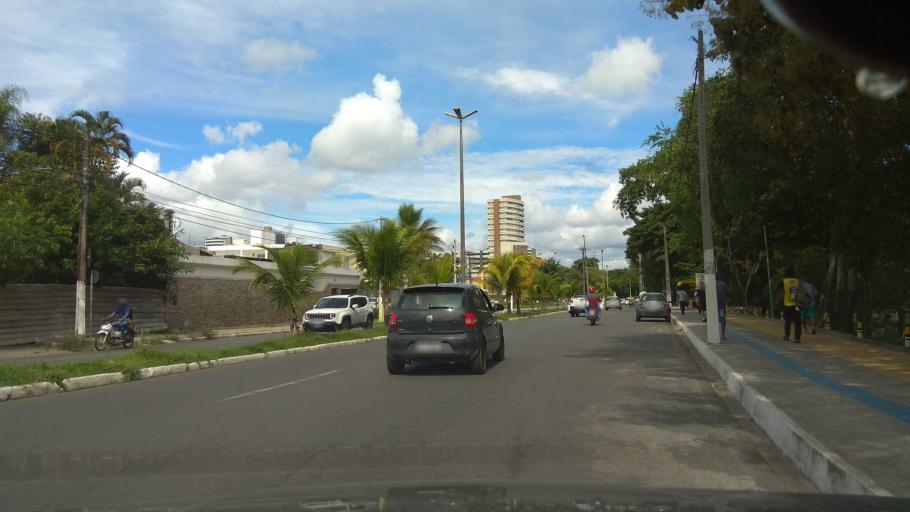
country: BR
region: Bahia
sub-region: Itabuna
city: Itabuna
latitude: -14.7937
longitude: -39.2736
